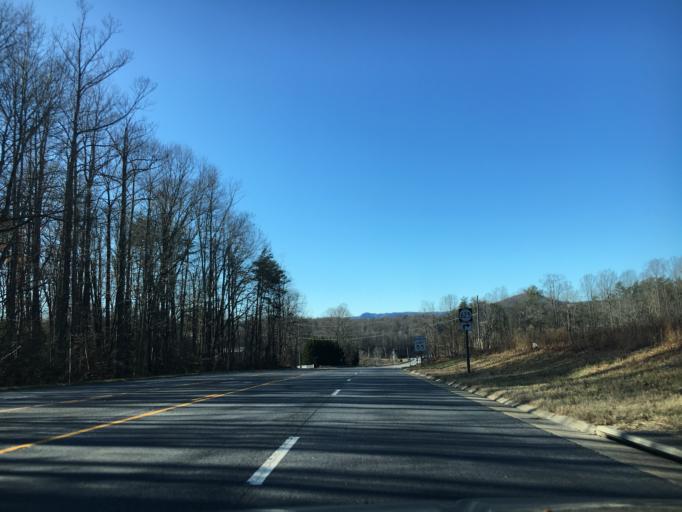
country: US
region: Virginia
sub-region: Patrick County
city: Patrick Springs
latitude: 36.6358
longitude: -80.2106
